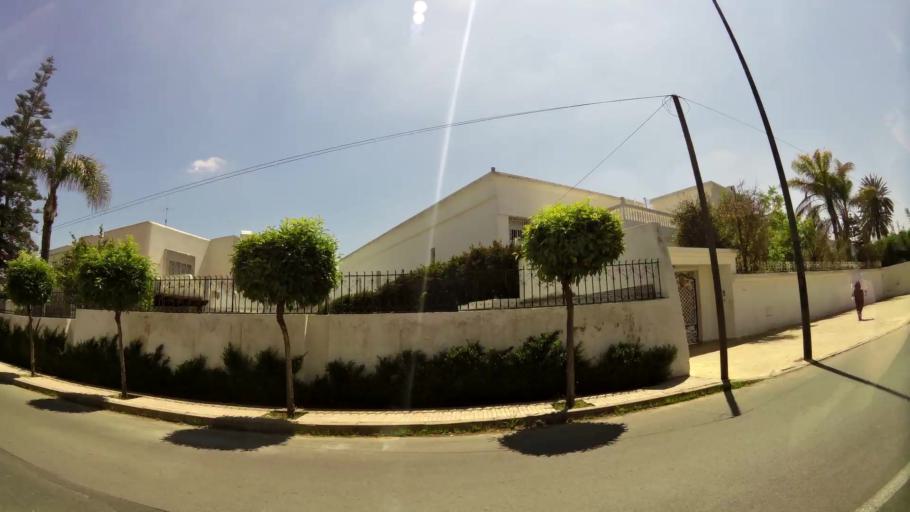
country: MA
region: Fes-Boulemane
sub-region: Fes
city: Fes
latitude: 34.0294
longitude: -5.0144
